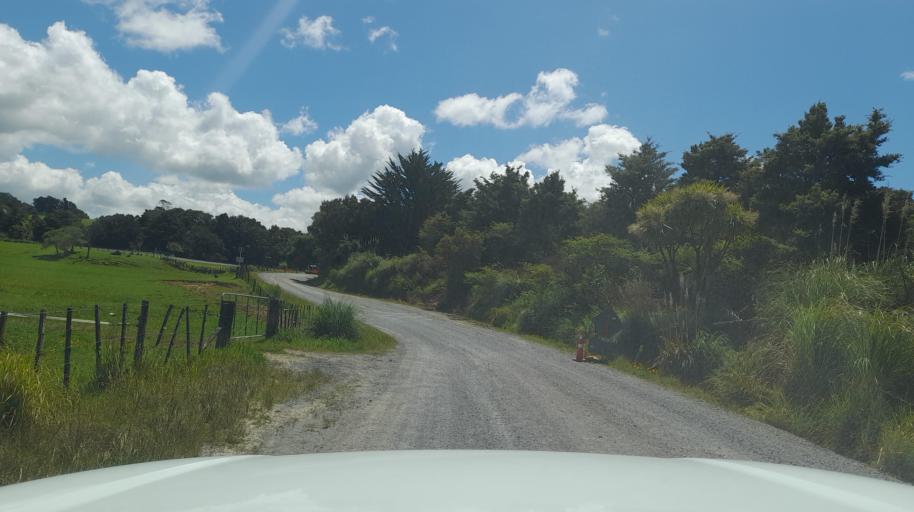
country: NZ
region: Northland
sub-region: Far North District
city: Kaitaia
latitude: -35.1065
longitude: 173.3916
